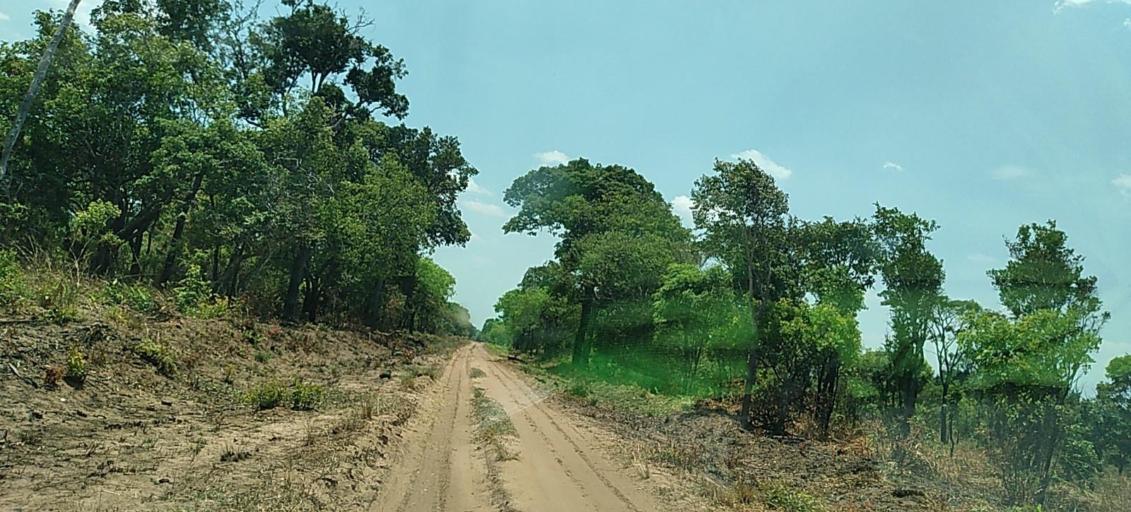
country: CD
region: Katanga
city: Kolwezi
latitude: -11.3868
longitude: 25.2203
